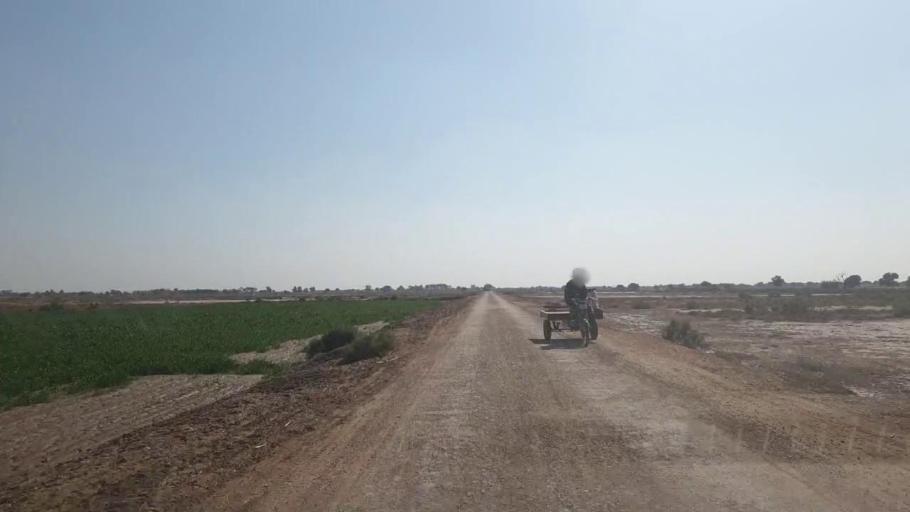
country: PK
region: Sindh
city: Chambar
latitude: 25.3015
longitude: 68.7418
